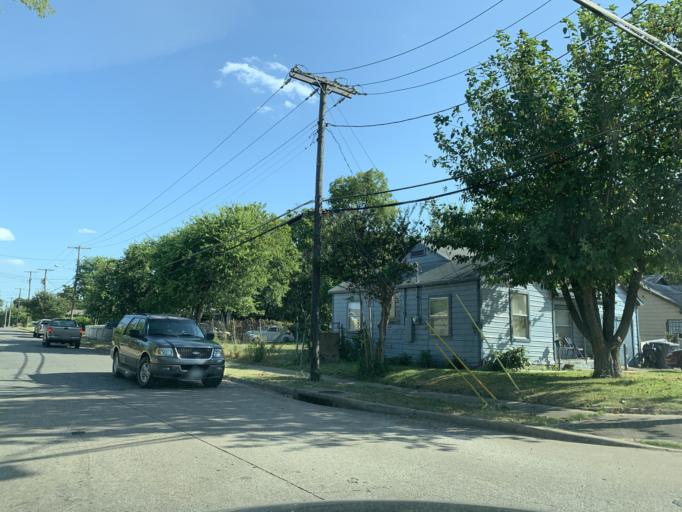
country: US
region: Texas
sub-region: Dallas County
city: Dallas
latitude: 32.7012
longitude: -96.7935
